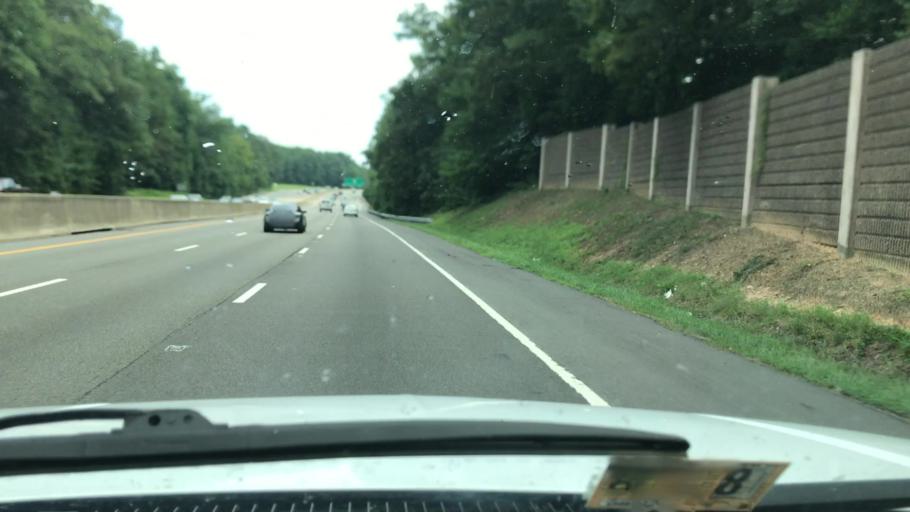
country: US
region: Virginia
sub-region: Chesterfield County
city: Bensley
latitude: 37.4653
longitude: -77.5039
